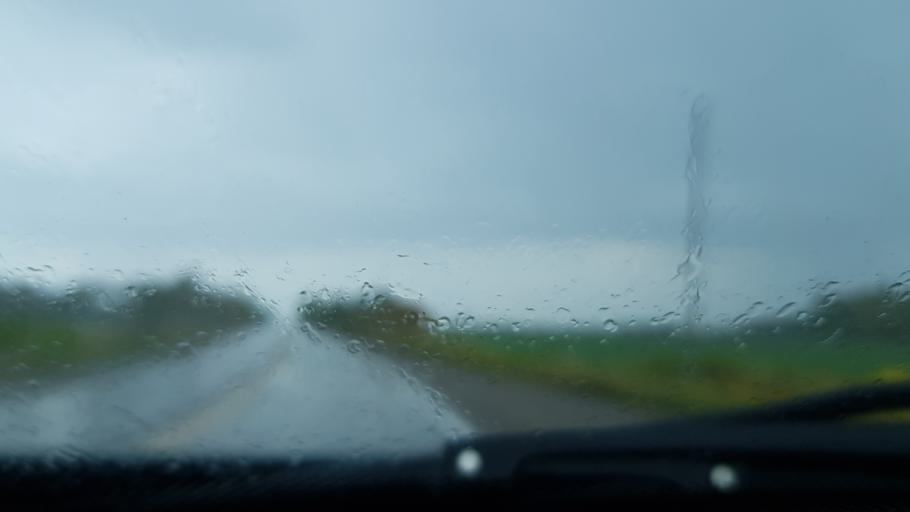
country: CA
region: Ontario
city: Omemee
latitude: 44.3927
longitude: -78.5564
